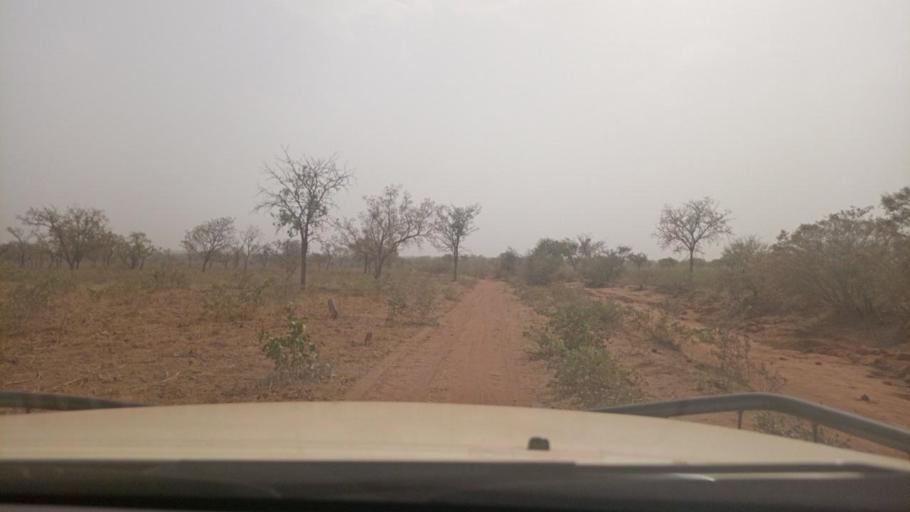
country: BF
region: Boucle du Mouhoun
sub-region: Province des Banwa
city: Salanso
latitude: 12.1639
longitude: -4.2382
